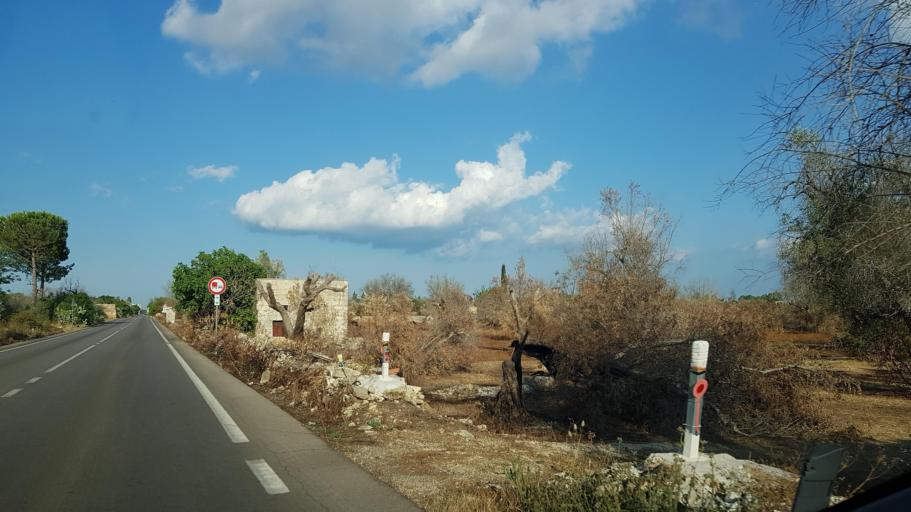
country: IT
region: Apulia
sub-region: Provincia di Lecce
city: Miggiano
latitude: 39.9643
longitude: 18.2958
